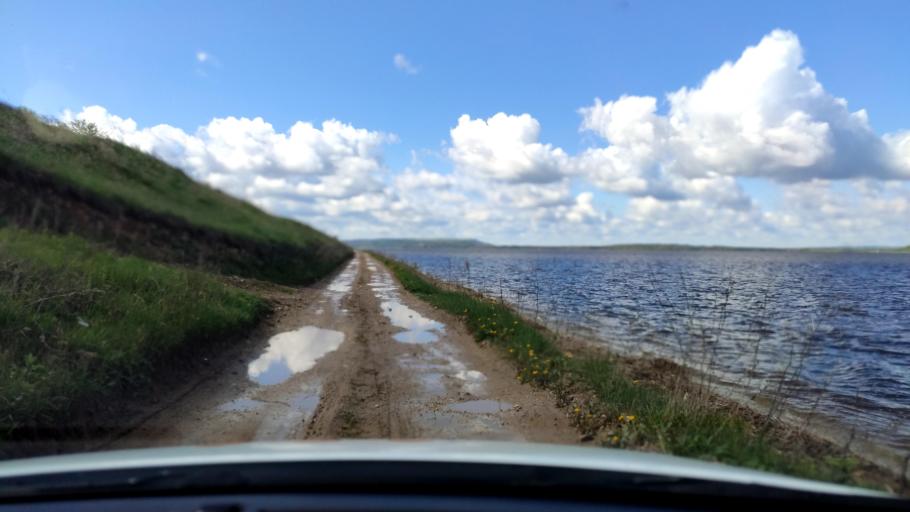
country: RU
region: Tatarstan
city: Sviyazhsk
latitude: 55.7752
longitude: 48.6903
